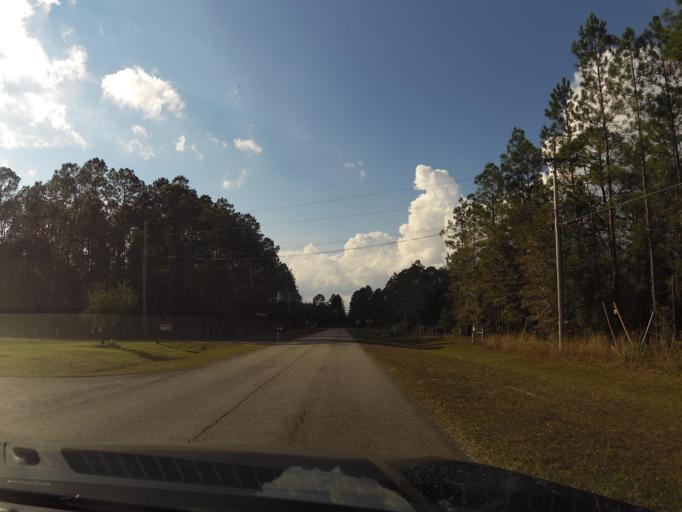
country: US
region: Florida
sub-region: Duval County
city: Baldwin
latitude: 30.1577
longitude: -81.9983
